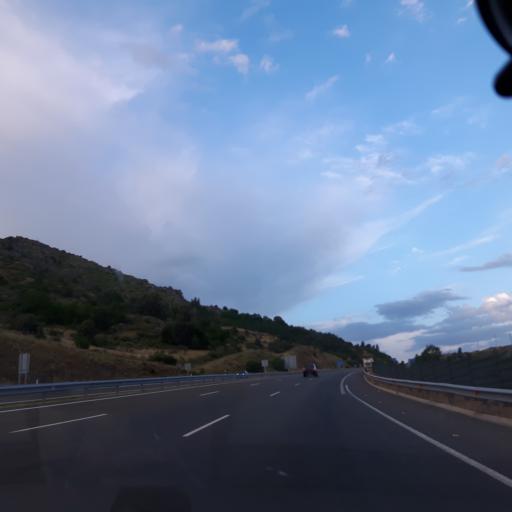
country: ES
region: Castille and Leon
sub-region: Provincia de Salamanca
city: Fresnedoso
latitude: 40.4305
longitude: -5.6964
